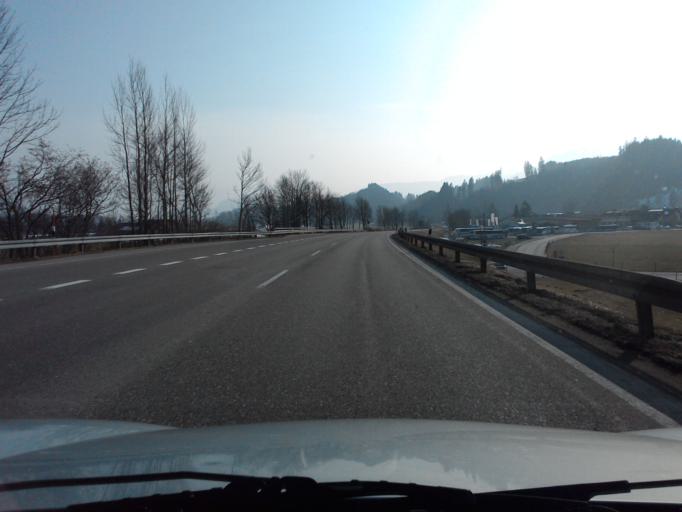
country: DE
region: Bavaria
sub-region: Swabia
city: Sonthofen
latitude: 47.5066
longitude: 10.2710
